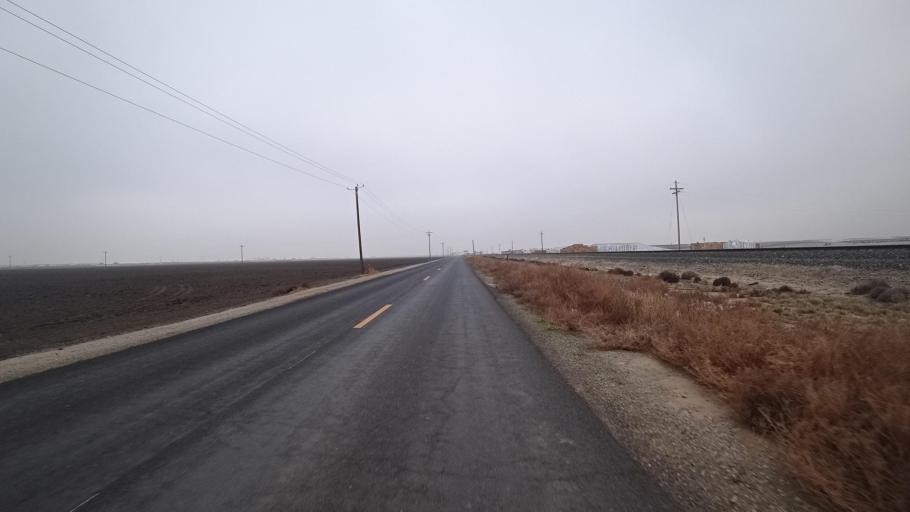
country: US
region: California
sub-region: Kern County
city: Greenfield
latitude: 35.1800
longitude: -119.1259
